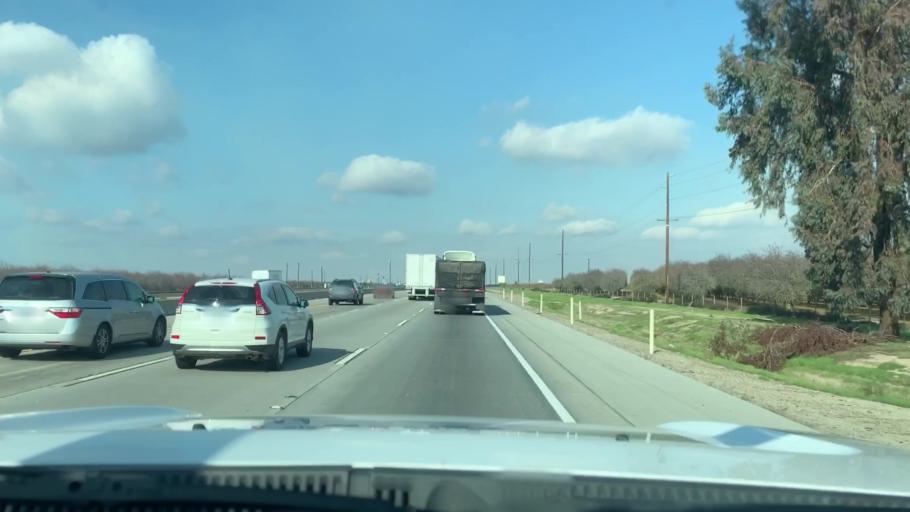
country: US
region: California
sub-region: Kern County
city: Shafter
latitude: 35.5414
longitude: -119.1940
